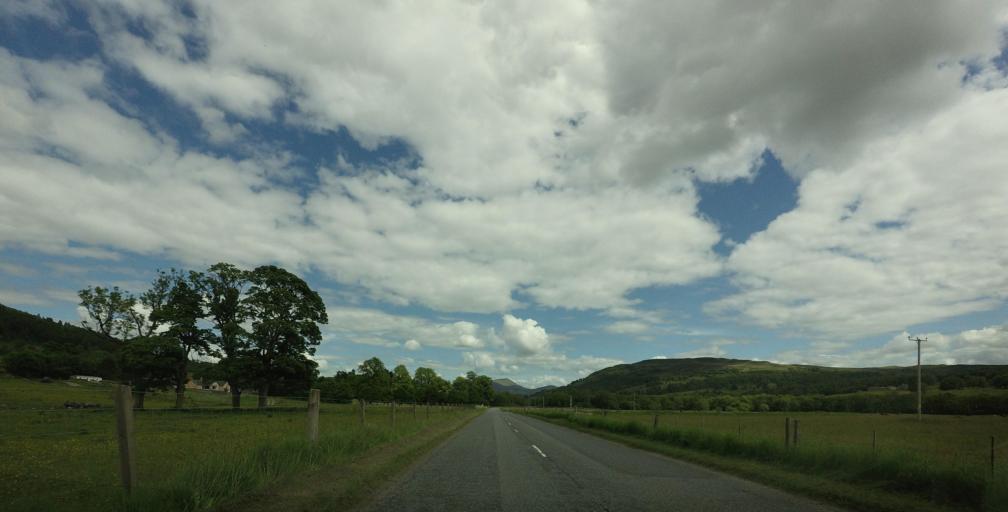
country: GB
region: Scotland
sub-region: Perth and Kinross
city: Aberfeldy
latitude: 56.7700
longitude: -3.9096
